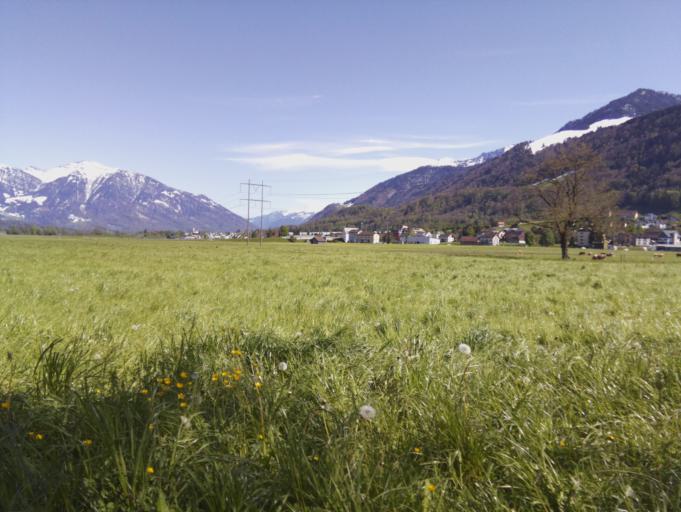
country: CH
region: Schwyz
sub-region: Bezirk March
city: Schubelbach
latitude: 47.1796
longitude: 8.9344
